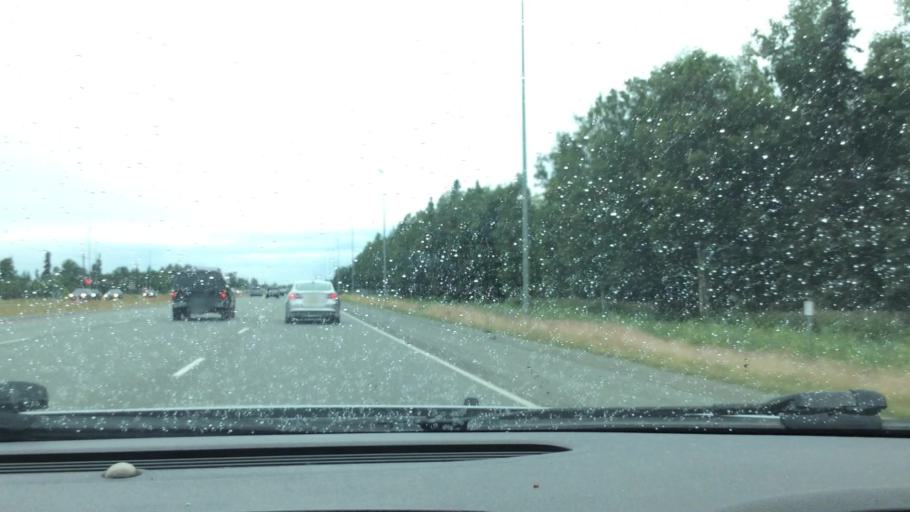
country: US
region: Alaska
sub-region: Anchorage Municipality
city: Elmendorf Air Force Base
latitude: 61.2247
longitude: -149.7527
